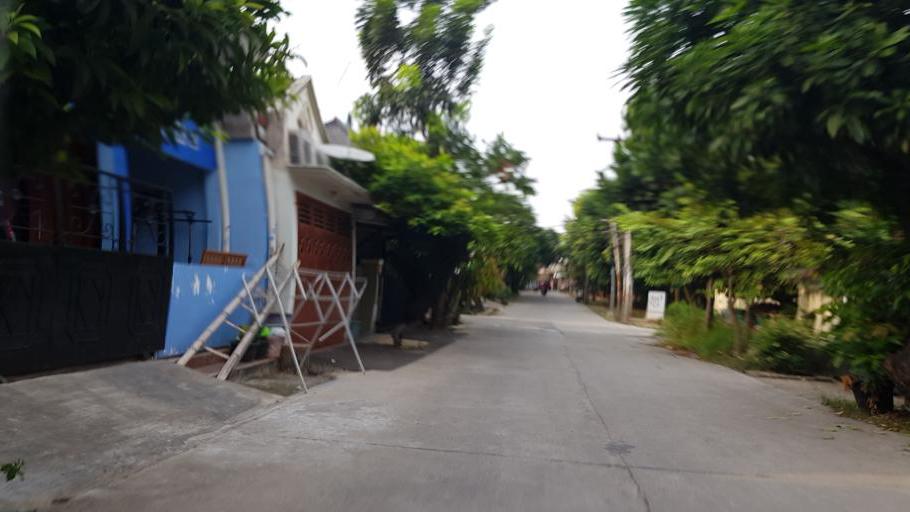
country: ID
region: West Java
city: Depok
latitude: -6.3715
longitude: 106.7952
